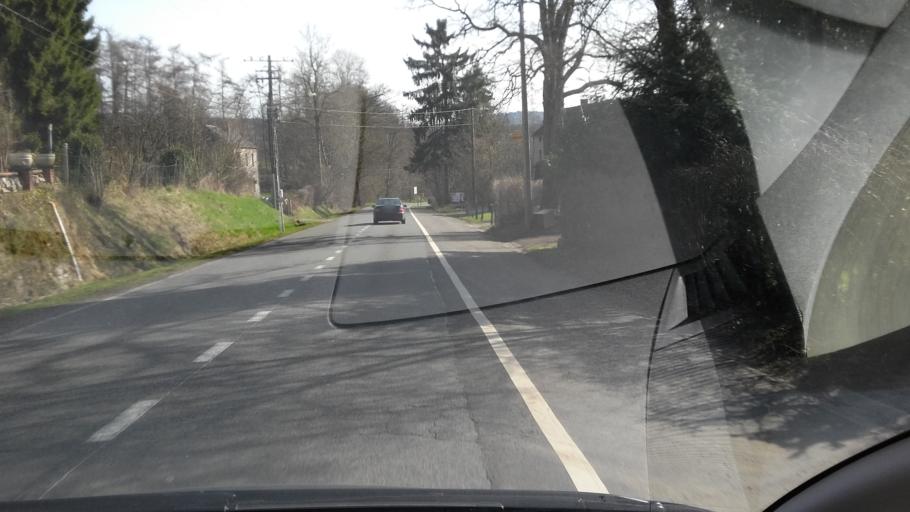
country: BE
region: Wallonia
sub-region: Province de Liege
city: Ferrieres
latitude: 50.4106
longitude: 5.6002
